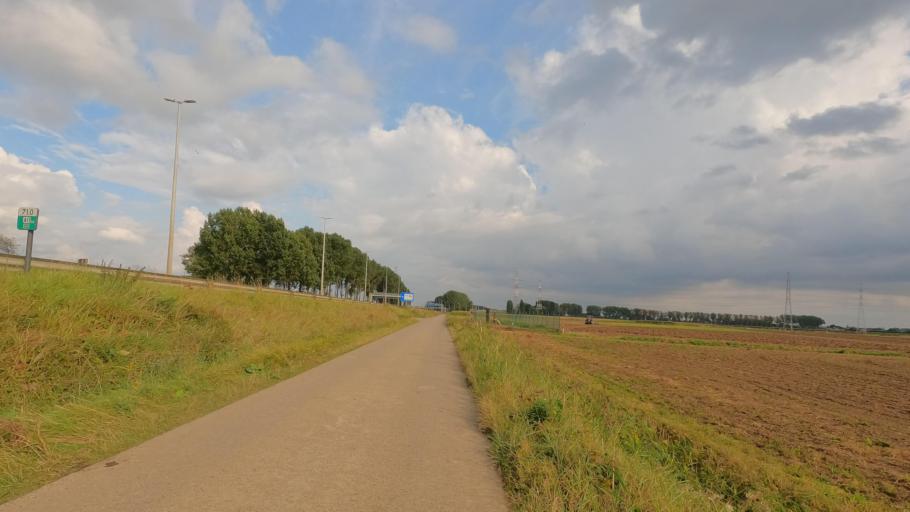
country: BE
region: Flanders
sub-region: Provincie Oost-Vlaanderen
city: Beveren
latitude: 51.2356
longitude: 4.2599
